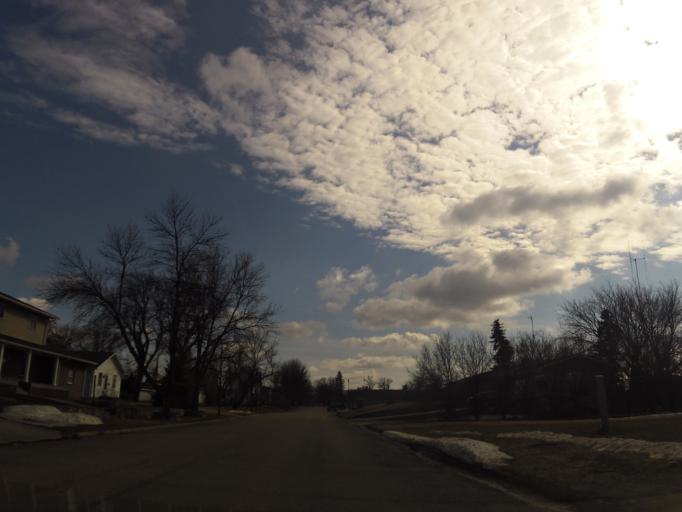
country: US
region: North Dakota
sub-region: Walsh County
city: Grafton
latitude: 48.4215
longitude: -97.4156
